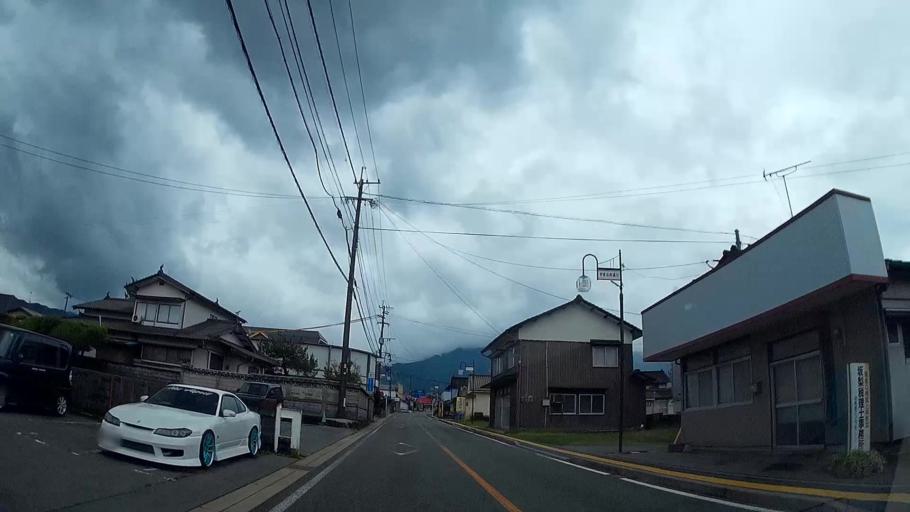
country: JP
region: Kumamoto
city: Aso
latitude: 32.9403
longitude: 131.1175
